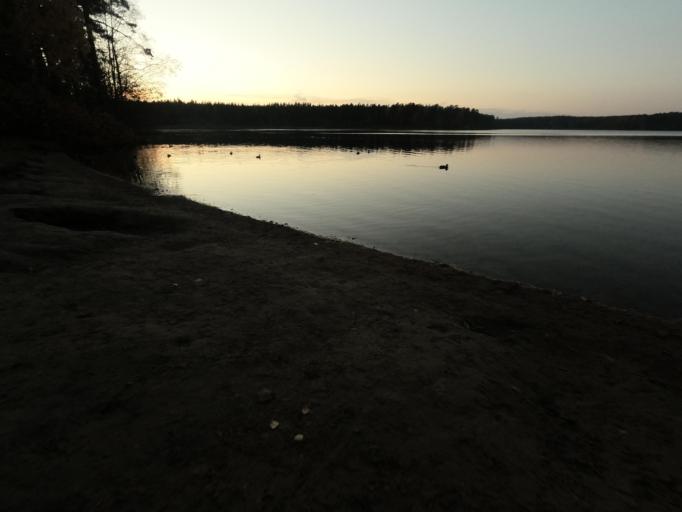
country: RU
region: St.-Petersburg
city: Komarovo
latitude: 60.2081
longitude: 29.7879
